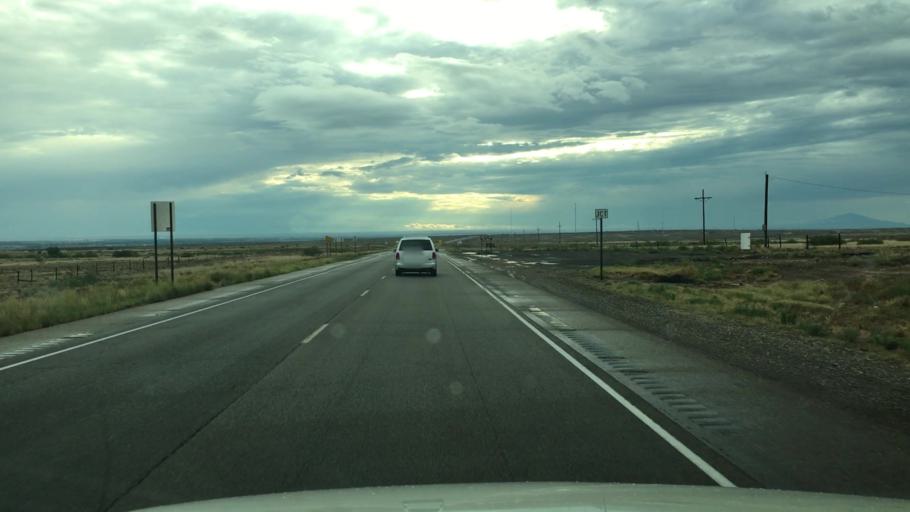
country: US
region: New Mexico
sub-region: Chaves County
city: Roswell
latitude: 33.3999
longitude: -104.3430
